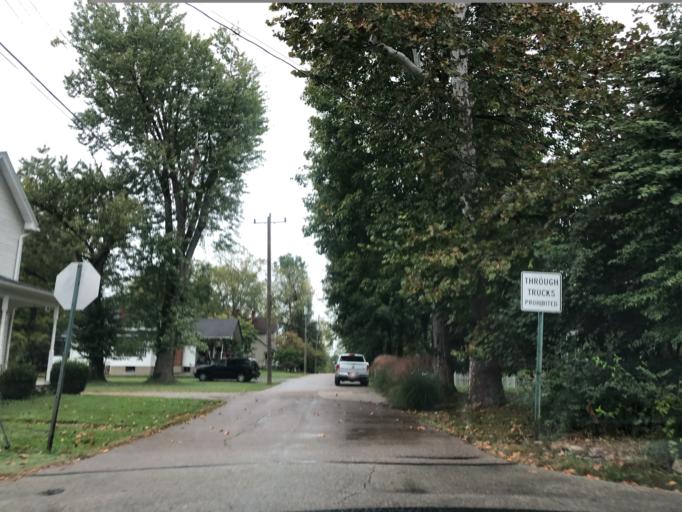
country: US
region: Ohio
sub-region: Hamilton County
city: Loveland
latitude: 39.2635
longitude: -84.2574
